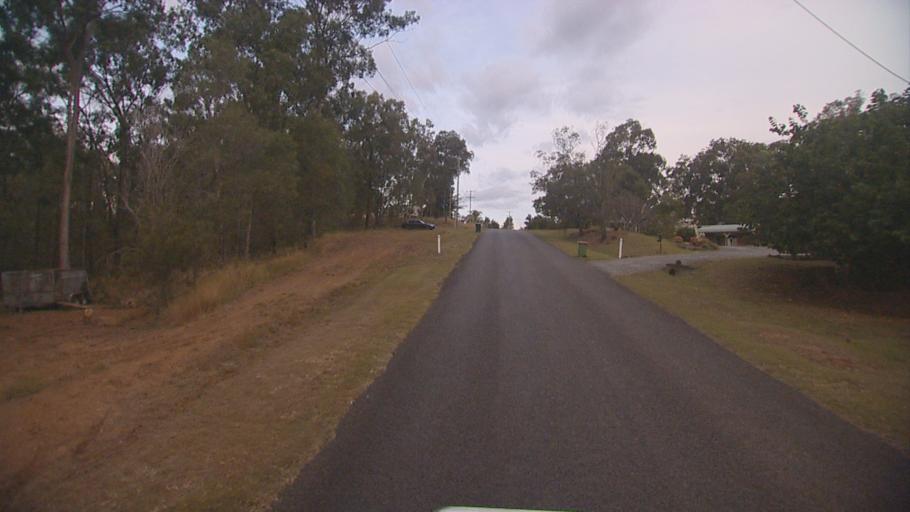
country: AU
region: Queensland
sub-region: Logan
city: Chambers Flat
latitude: -27.8216
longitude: 153.0944
